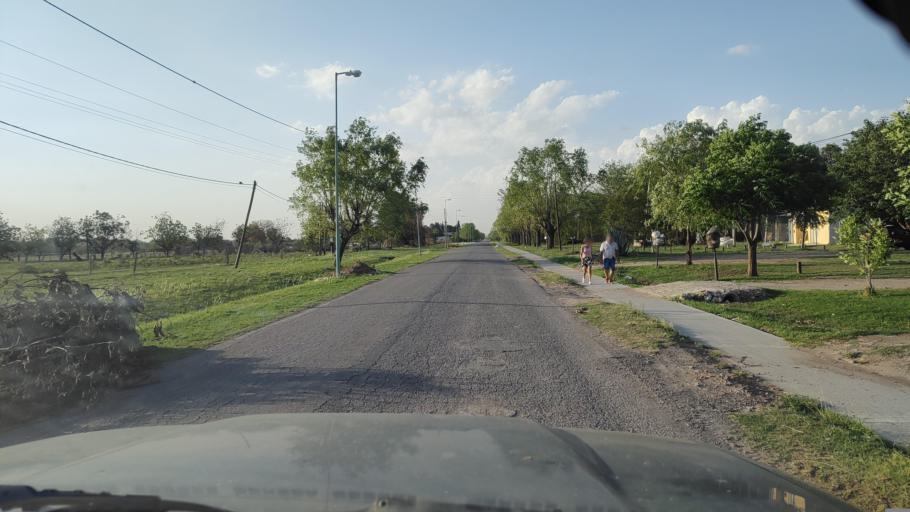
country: AR
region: Buenos Aires
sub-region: Partido de Lujan
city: Lujan
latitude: -34.5539
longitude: -59.2059
